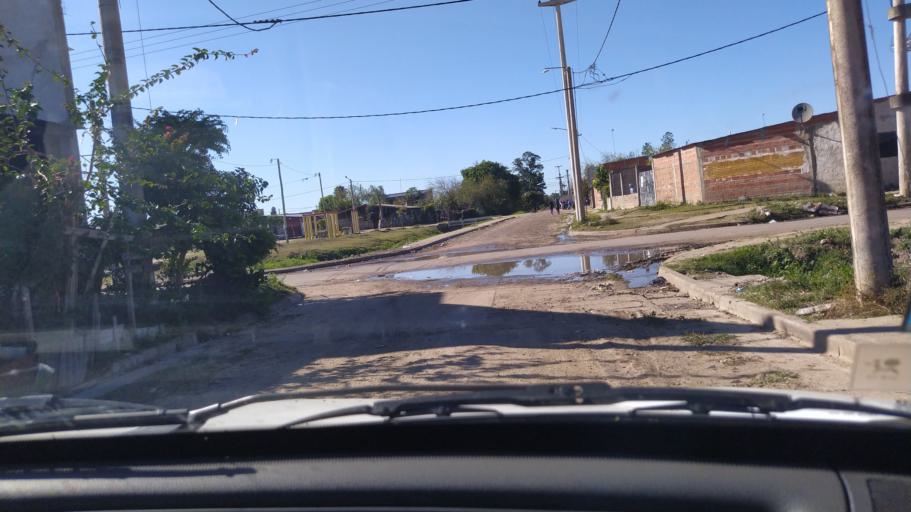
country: AR
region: Corrientes
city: Corrientes
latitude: -27.4980
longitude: -58.8083
